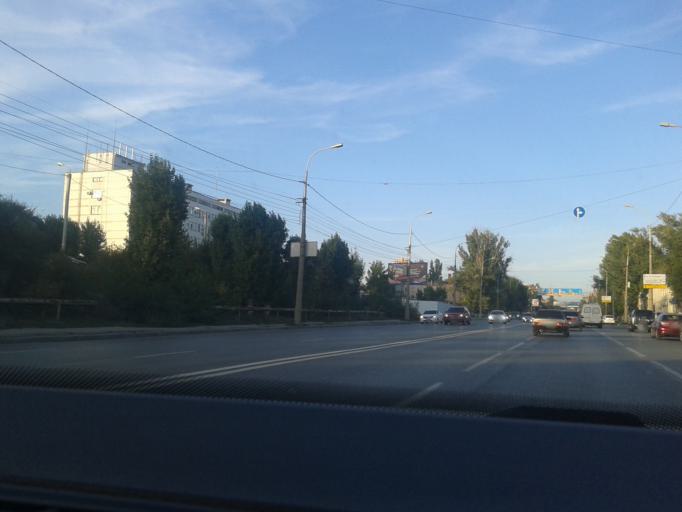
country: RU
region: Volgograd
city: Volgograd
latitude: 48.7116
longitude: 44.4941
